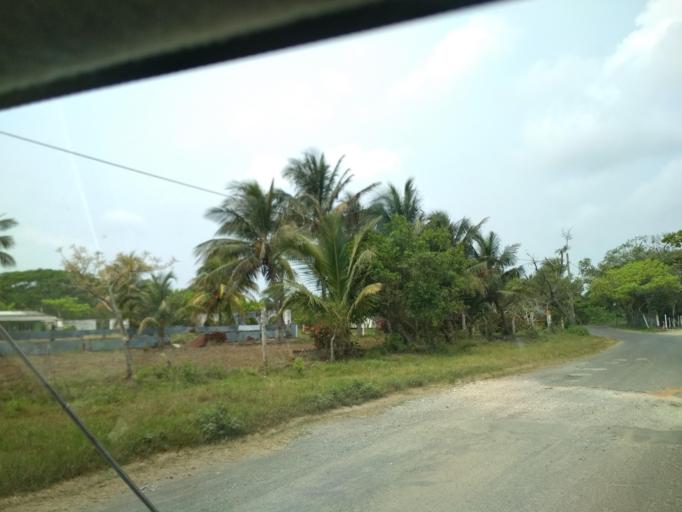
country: MX
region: Veracruz
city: Anton Lizardo
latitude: 19.0392
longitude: -95.9759
